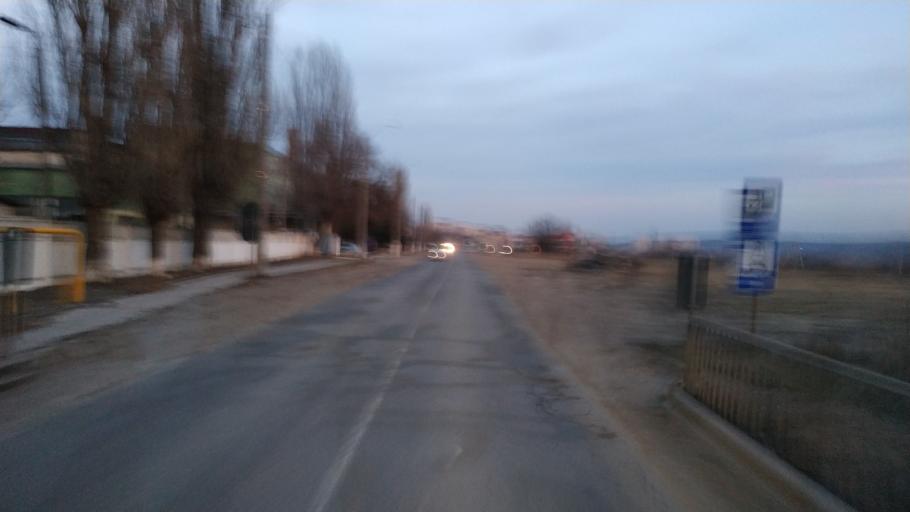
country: MD
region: Laloveni
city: Ialoveni
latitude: 46.9520
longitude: 28.7636
